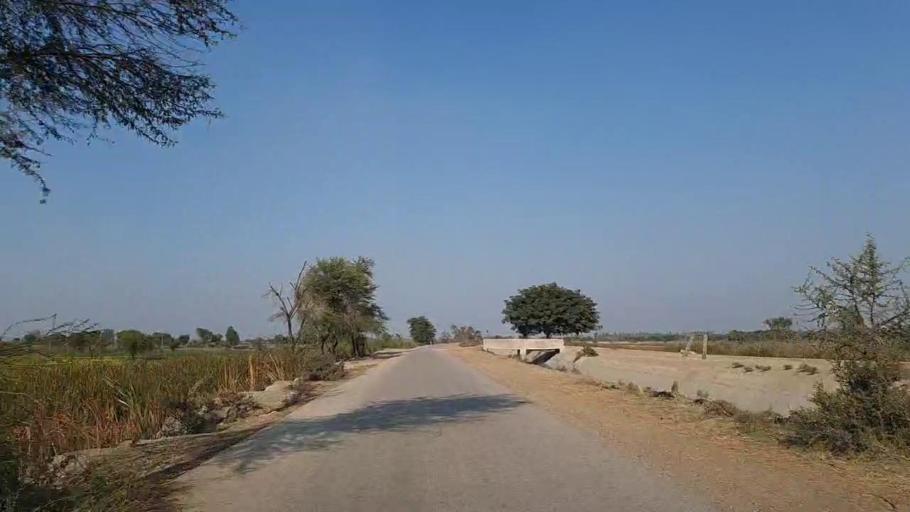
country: PK
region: Sindh
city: Daur
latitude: 26.4255
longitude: 68.2626
